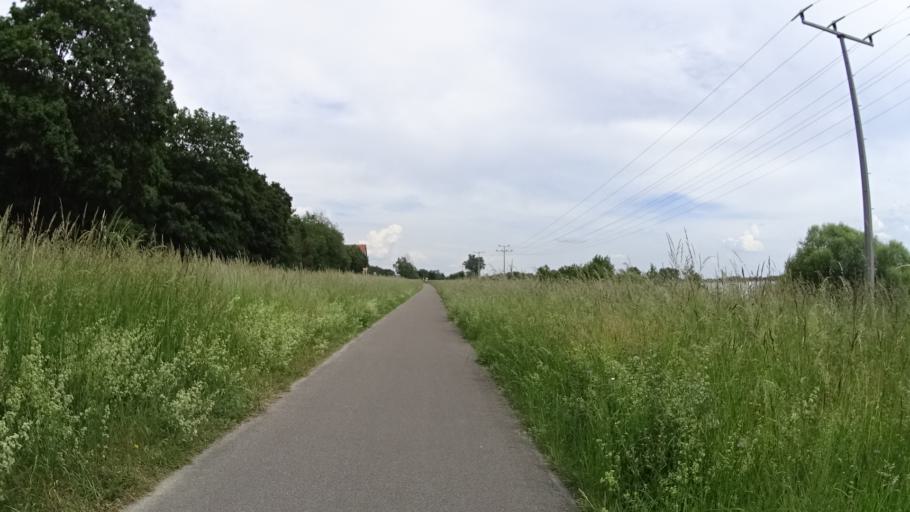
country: DE
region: Bavaria
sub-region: Upper Palatinate
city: Donaustauf
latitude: 49.0237
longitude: 12.2499
